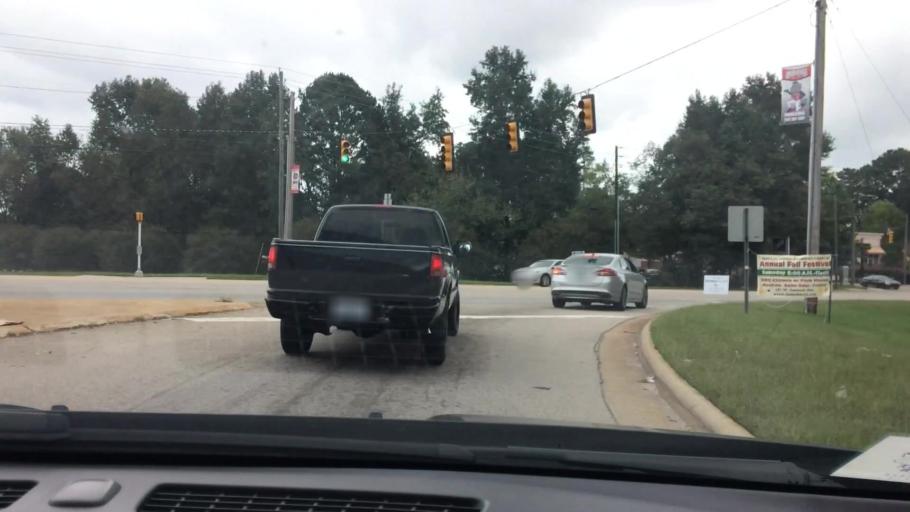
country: US
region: North Carolina
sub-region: Wake County
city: Zebulon
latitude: 35.8335
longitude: -78.3209
